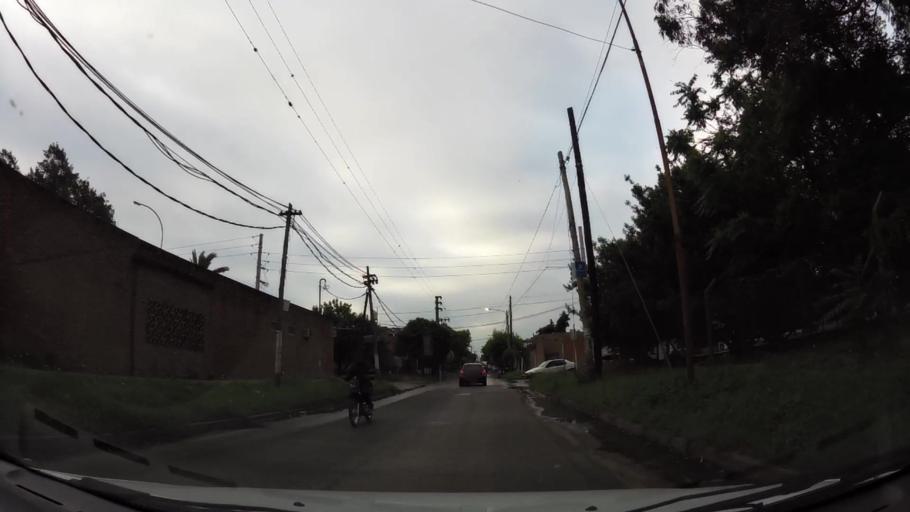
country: AR
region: Buenos Aires
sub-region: Partido de Moron
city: Moron
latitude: -34.6803
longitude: -58.5994
